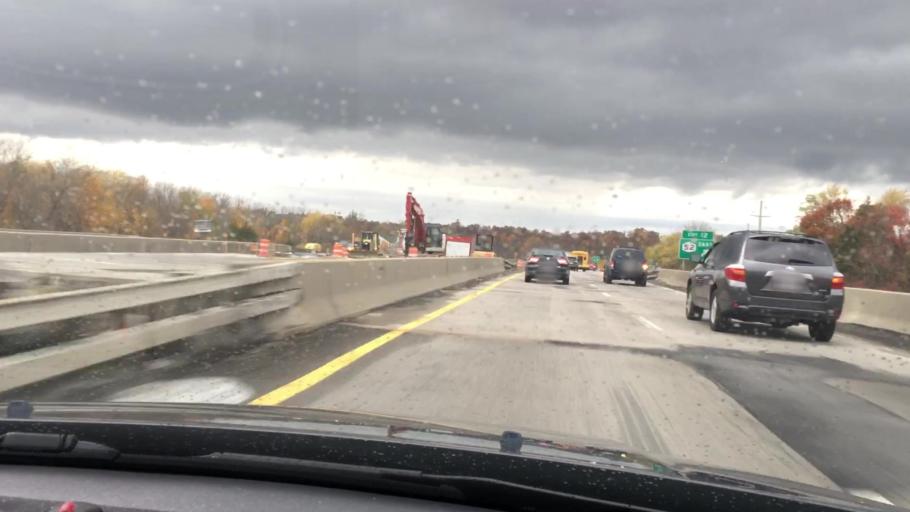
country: US
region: New York
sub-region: Dutchess County
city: Fishkill
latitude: 41.5251
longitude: -73.9121
